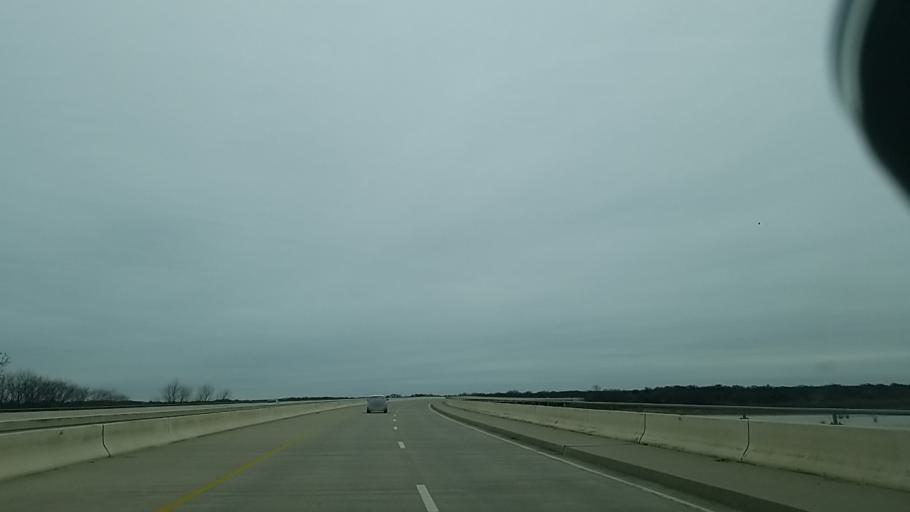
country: US
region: Texas
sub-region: Denton County
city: Copper Canyon
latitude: 33.1235
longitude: -97.0842
